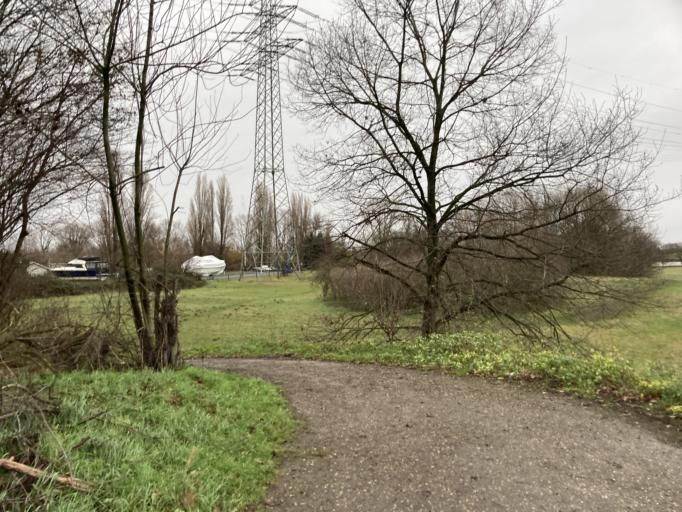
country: DE
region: North Rhine-Westphalia
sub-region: Regierungsbezirk Dusseldorf
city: Meerbusch
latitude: 51.3347
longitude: 6.6933
